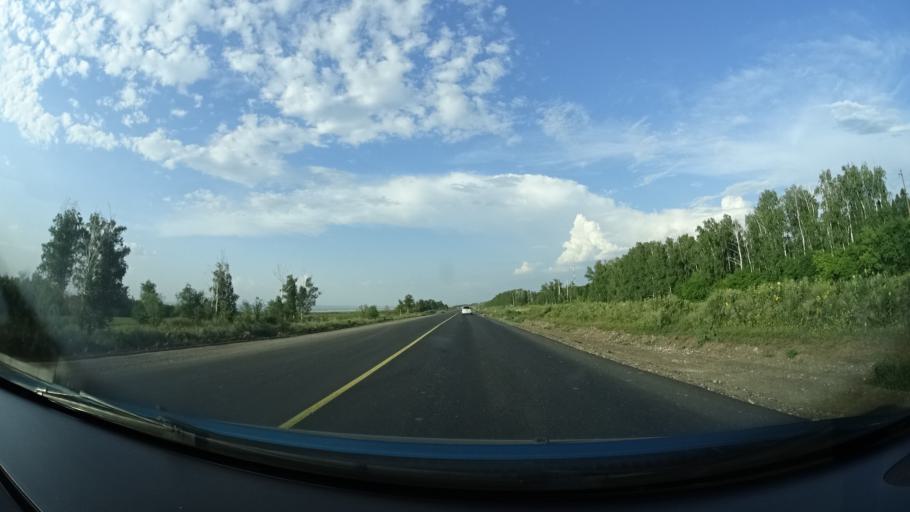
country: RU
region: Samara
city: Sukhodol
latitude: 53.7530
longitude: 50.8709
